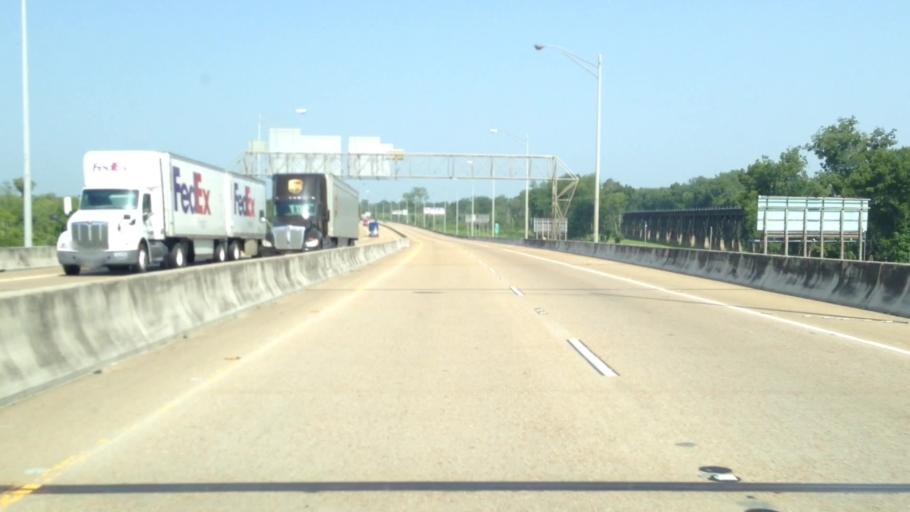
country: US
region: Mississippi
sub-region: Warren County
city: Vicksburg
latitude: 32.3174
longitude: -90.9126
